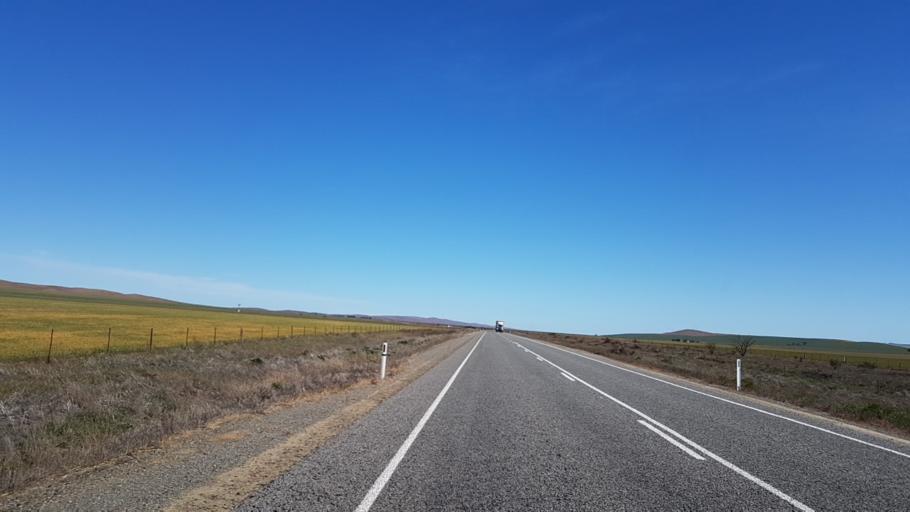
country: AU
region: South Australia
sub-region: Northern Areas
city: Jamestown
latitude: -33.2622
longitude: 138.8698
